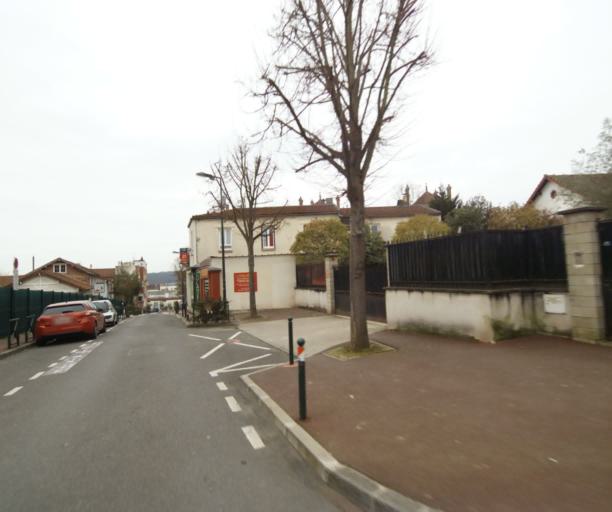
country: FR
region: Ile-de-France
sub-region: Departement des Hauts-de-Seine
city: Garches
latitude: 48.8469
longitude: 2.1893
